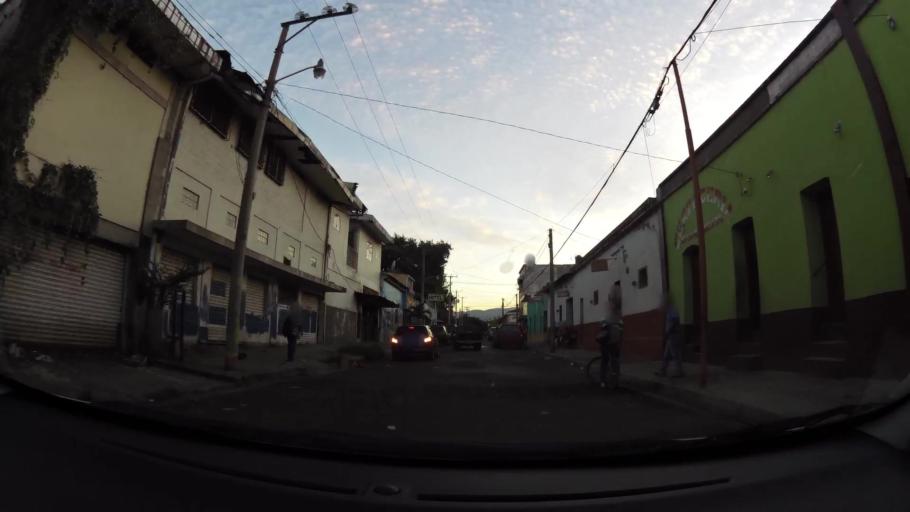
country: SV
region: Santa Ana
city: Santa Ana
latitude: 13.9918
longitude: -89.5634
